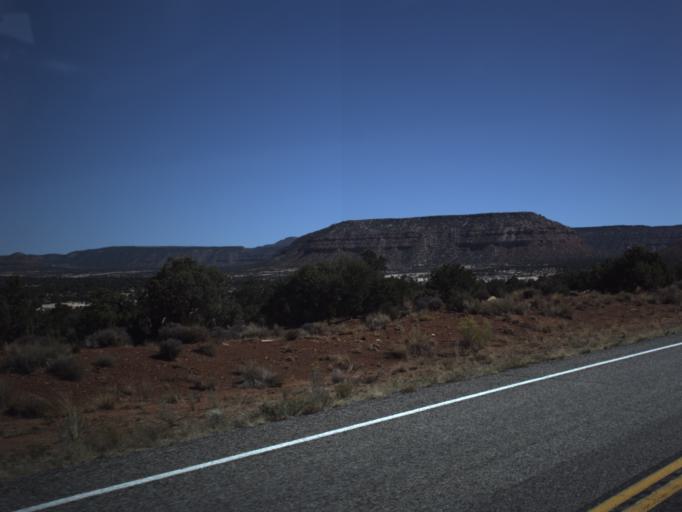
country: US
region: Utah
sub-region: San Juan County
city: Blanding
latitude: 37.6514
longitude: -110.1232
